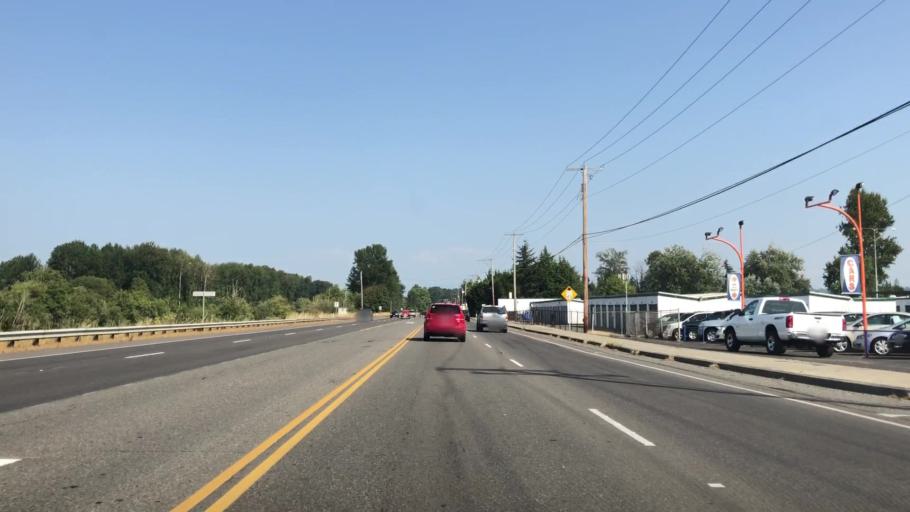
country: US
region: Washington
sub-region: Pierce County
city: Waller
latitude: 47.2087
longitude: -122.3290
